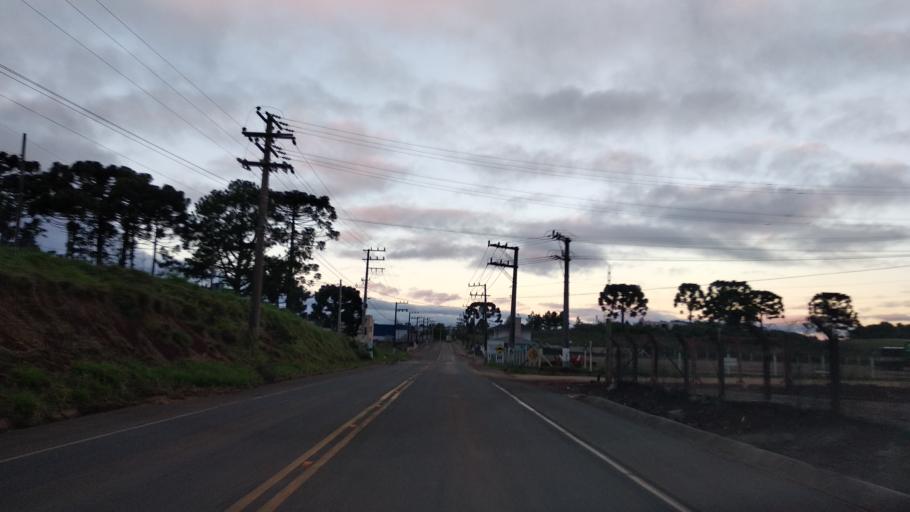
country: BR
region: Santa Catarina
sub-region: Campos Novos
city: Campos Novos
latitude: -27.3799
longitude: -51.2091
